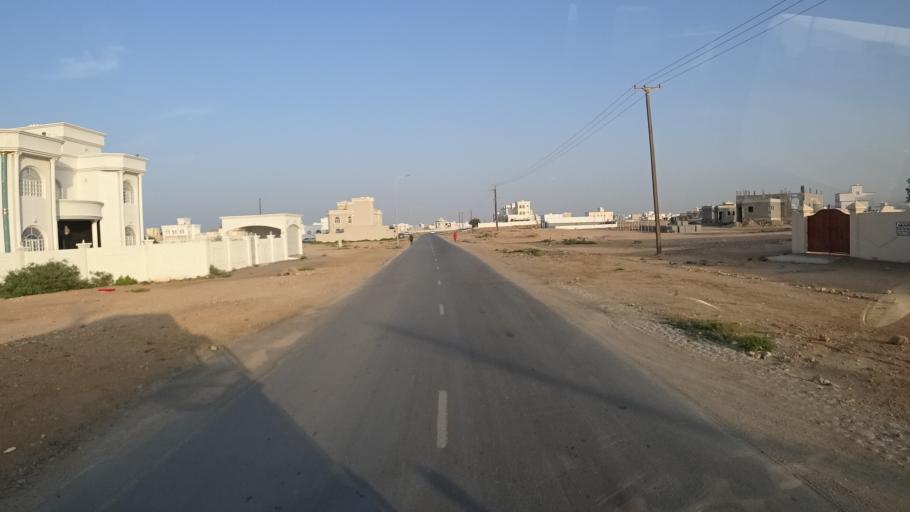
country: OM
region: Ash Sharqiyah
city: Sur
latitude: 22.6198
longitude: 59.4570
